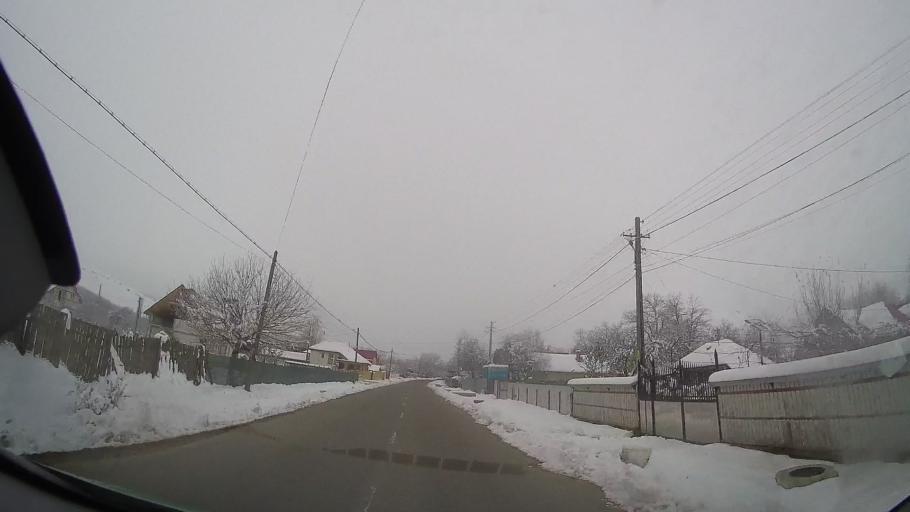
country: RO
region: Neamt
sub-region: Comuna Bozieni
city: Bozieni
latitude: 46.8367
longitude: 27.1554
